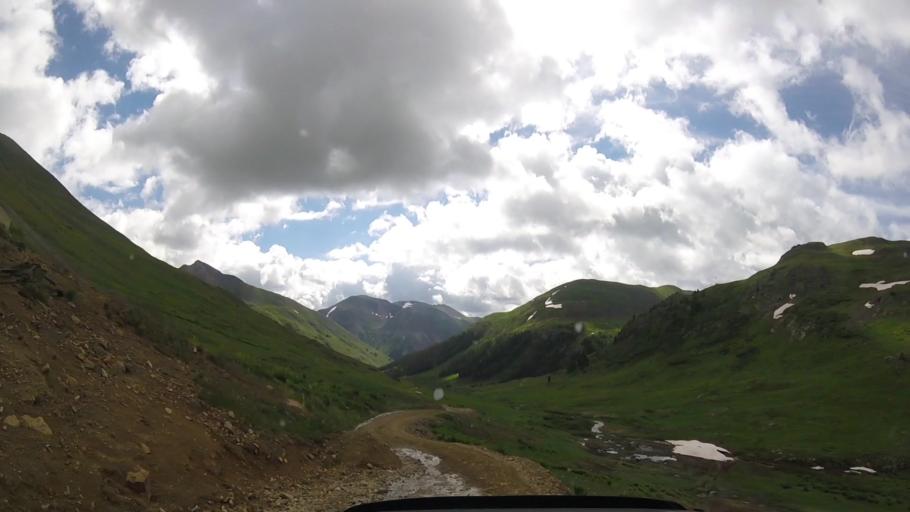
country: US
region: Colorado
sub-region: Ouray County
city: Ouray
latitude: 37.9332
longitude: -107.5973
